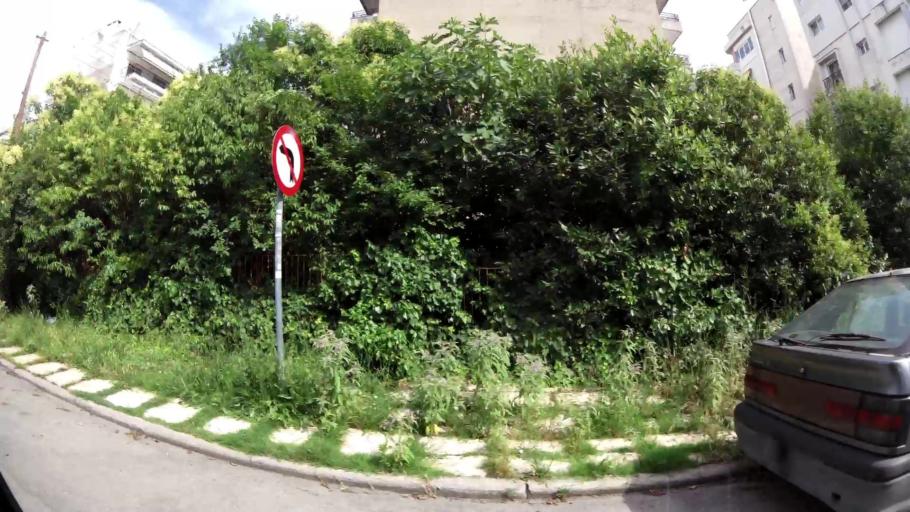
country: GR
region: Central Macedonia
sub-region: Nomos Thessalonikis
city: Kalamaria
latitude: 40.5864
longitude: 22.9432
